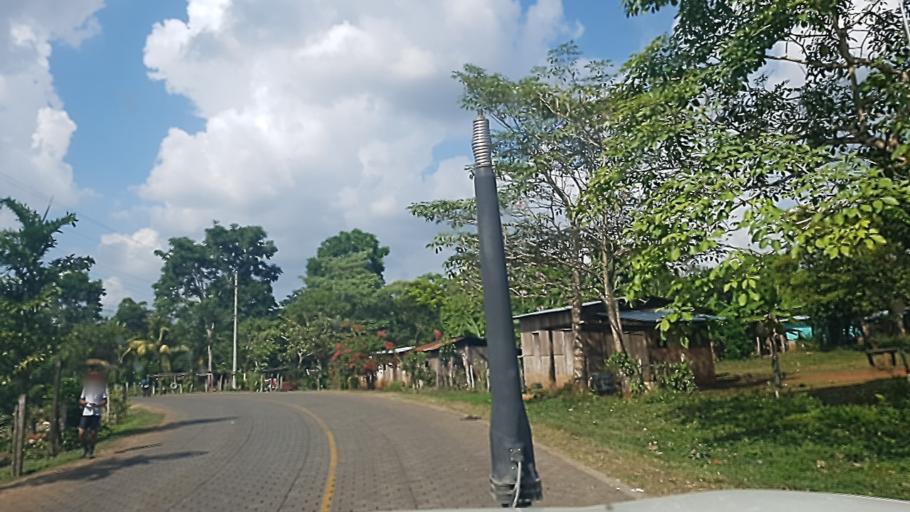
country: NI
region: Atlantico Sur
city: Nueva Guinea
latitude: 11.7021
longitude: -84.3726
